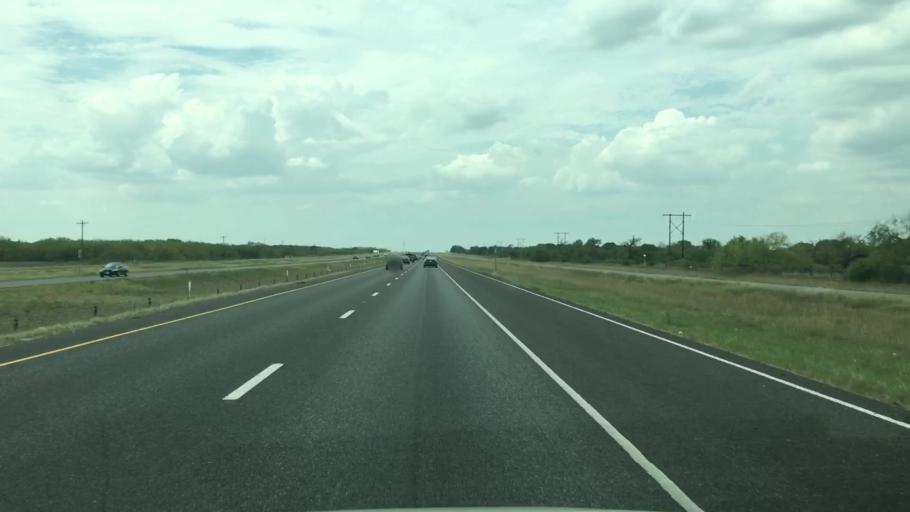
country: US
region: Texas
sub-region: Atascosa County
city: Pleasanton
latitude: 28.8054
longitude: -98.3463
